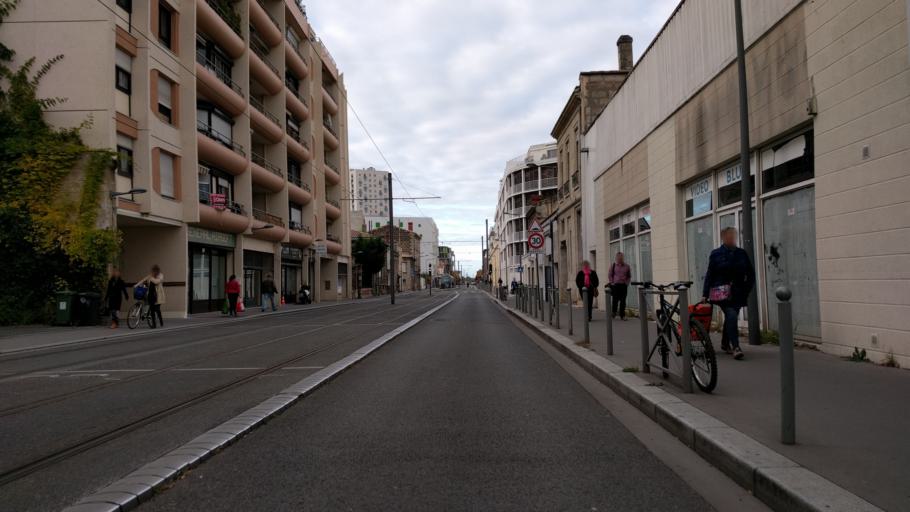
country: FR
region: Aquitaine
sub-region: Departement de la Gironde
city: Bordeaux
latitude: 44.8571
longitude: -0.5747
